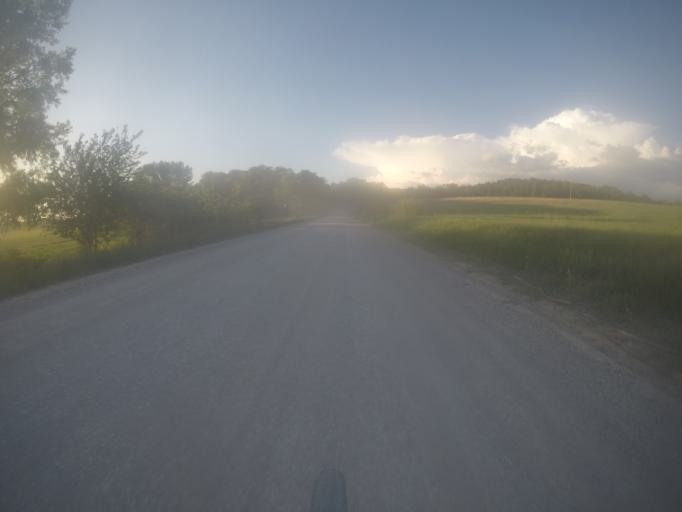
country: US
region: Kansas
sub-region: Riley County
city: Manhattan
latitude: 39.2299
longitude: -96.5479
